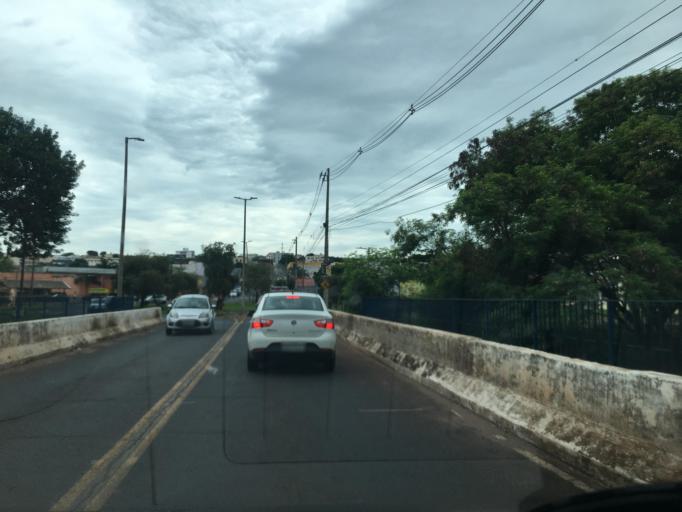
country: BR
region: Minas Gerais
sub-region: Uberlandia
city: Uberlandia
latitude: -18.9208
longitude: -48.3030
